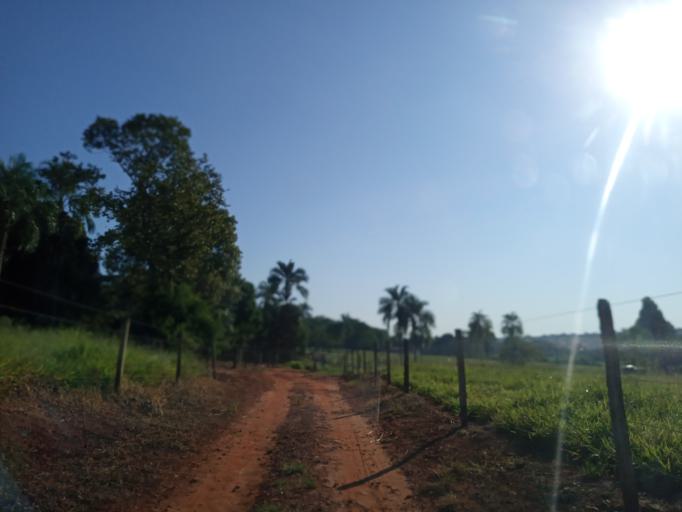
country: BR
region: Minas Gerais
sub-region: Ituiutaba
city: Ituiutaba
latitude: -18.9769
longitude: -49.4974
